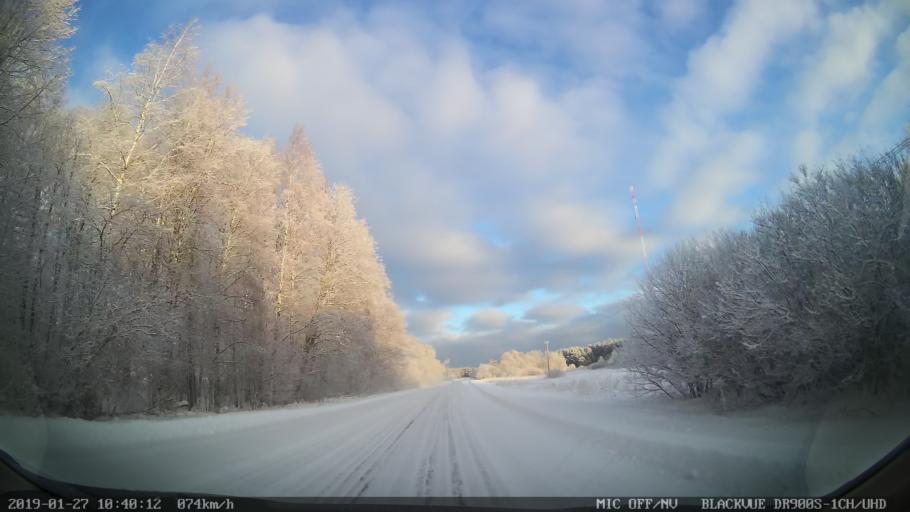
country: EE
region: Harju
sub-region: Raasiku vald
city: Raasiku
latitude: 59.5000
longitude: 25.2608
